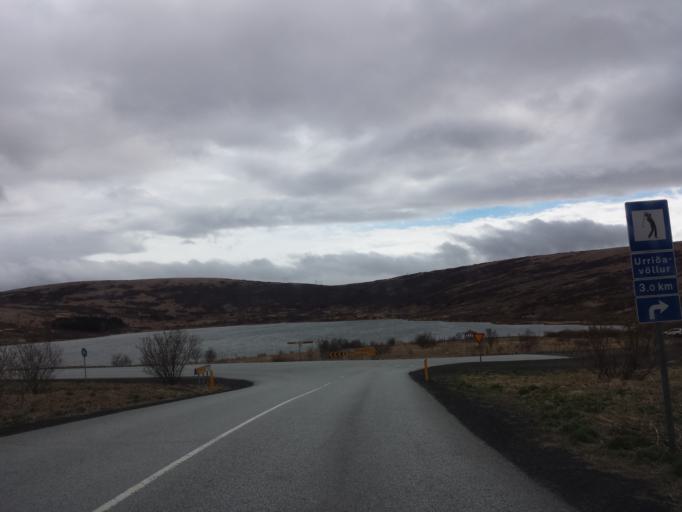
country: IS
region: Capital Region
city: Gardabaer
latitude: 64.0818
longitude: -21.8799
